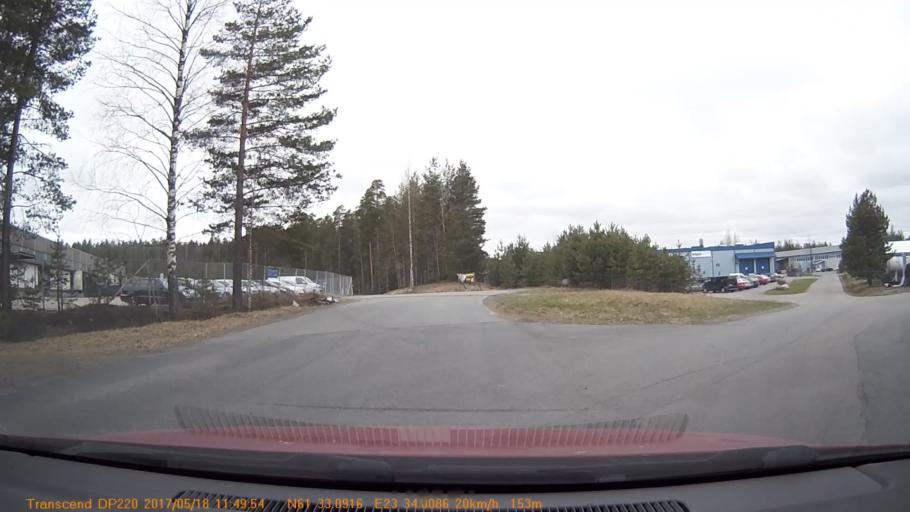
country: FI
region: Pirkanmaa
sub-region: Tampere
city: Yloejaervi
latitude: 61.5514
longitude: 23.5667
